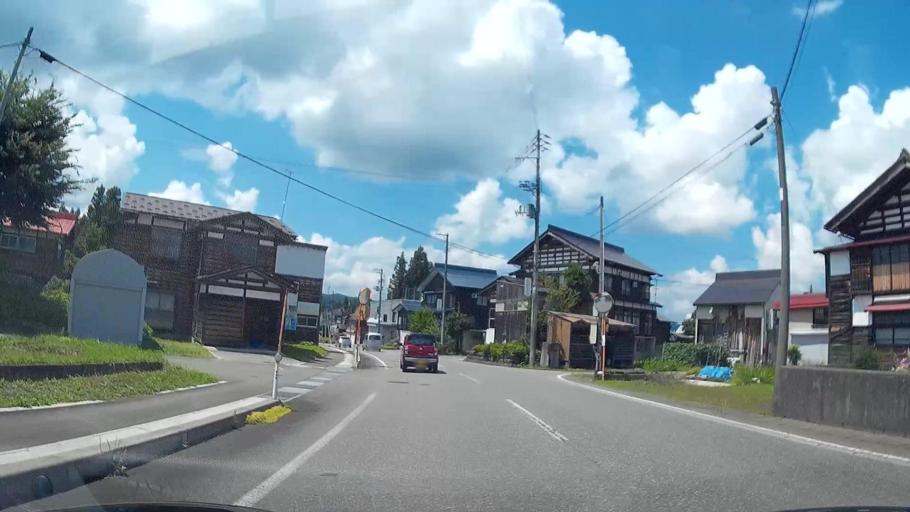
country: JP
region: Niigata
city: Tokamachi
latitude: 37.1004
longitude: 138.7373
